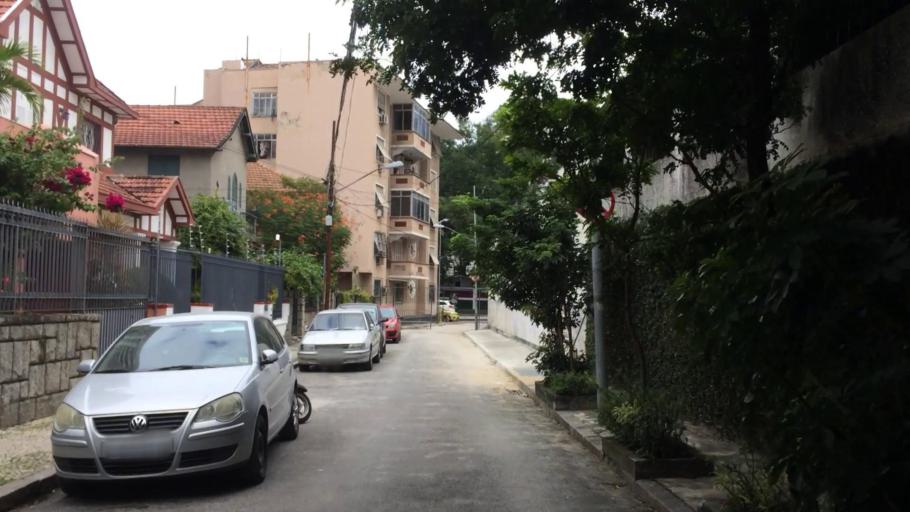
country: BR
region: Rio de Janeiro
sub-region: Rio De Janeiro
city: Rio de Janeiro
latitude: -22.9356
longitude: -43.1832
